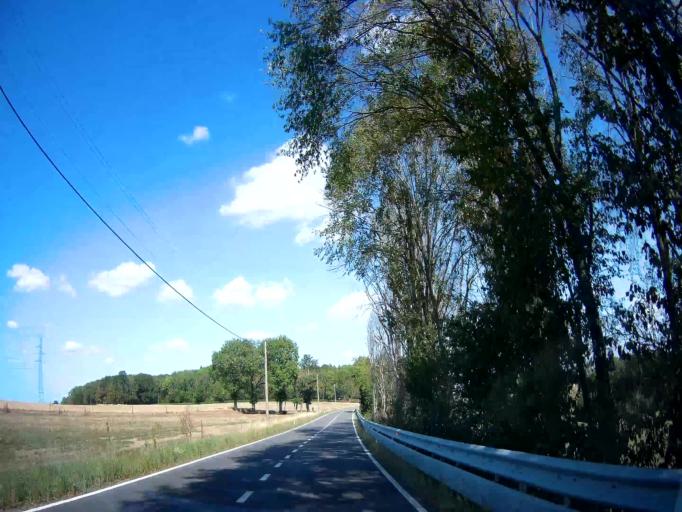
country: BE
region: Wallonia
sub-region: Province de Namur
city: Beauraing
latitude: 50.1807
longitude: 4.9242
